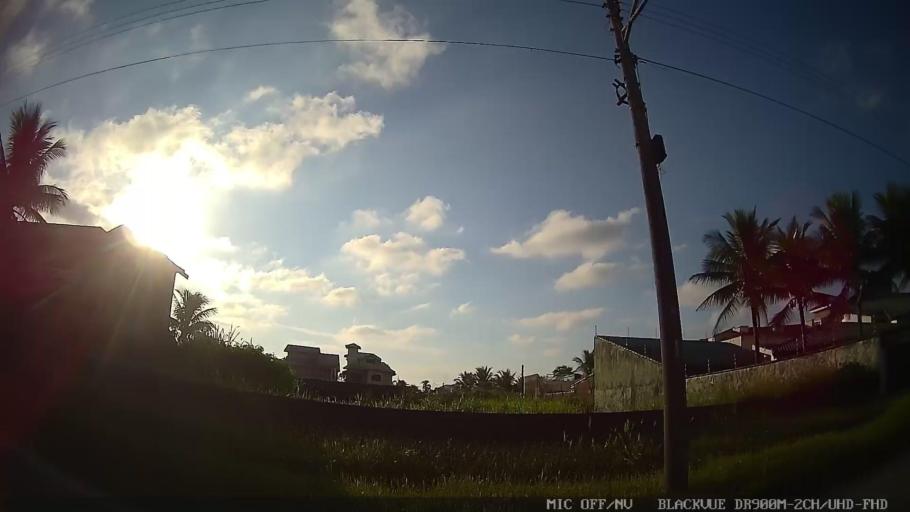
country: BR
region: Sao Paulo
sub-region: Peruibe
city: Peruibe
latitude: -24.2991
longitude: -46.9667
